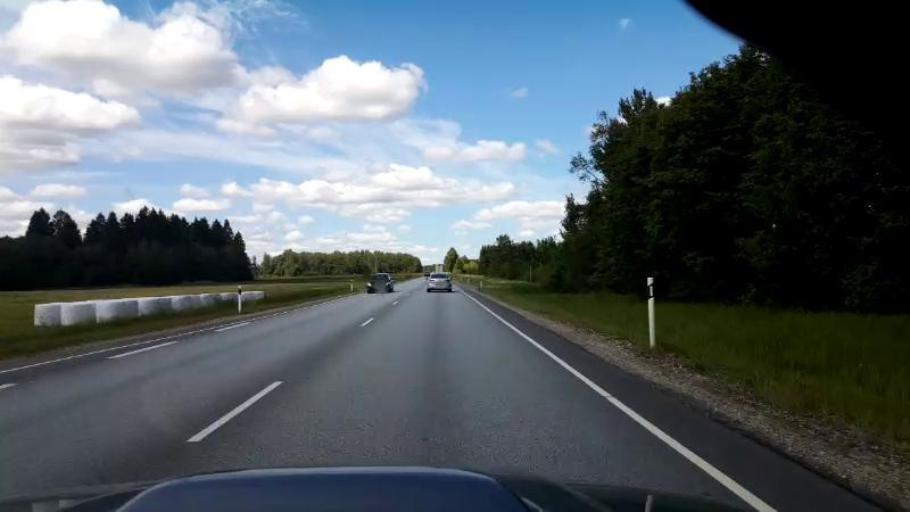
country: EE
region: Paernumaa
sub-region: Halinga vald
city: Parnu-Jaagupi
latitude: 58.5595
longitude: 24.5224
